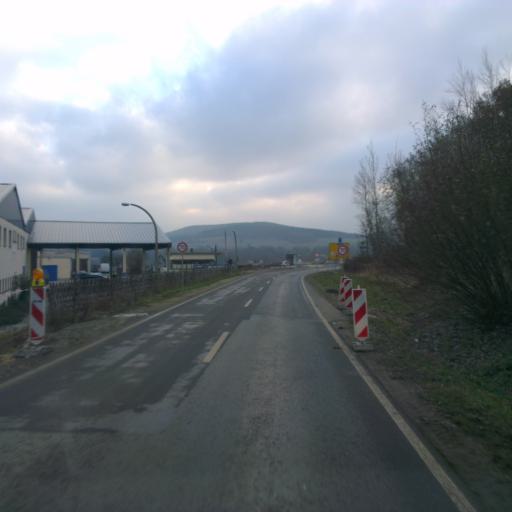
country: DE
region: Thuringia
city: Schops
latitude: 50.8343
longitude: 11.5895
